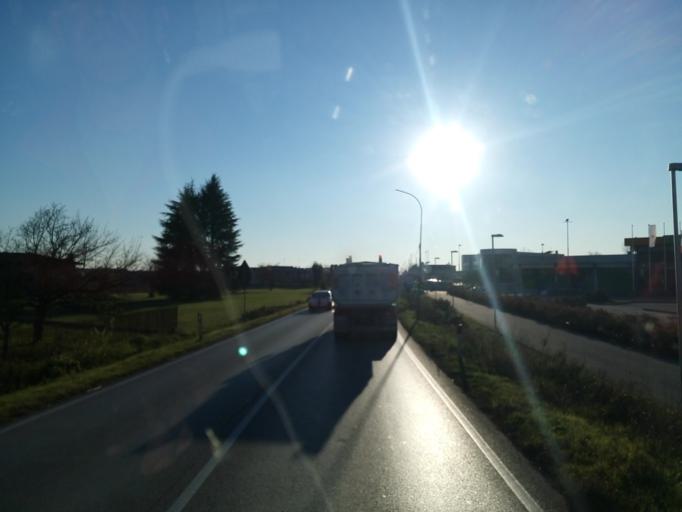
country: IT
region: Veneto
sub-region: Provincia di Treviso
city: Cornuda
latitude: 45.8126
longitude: 12.0123
